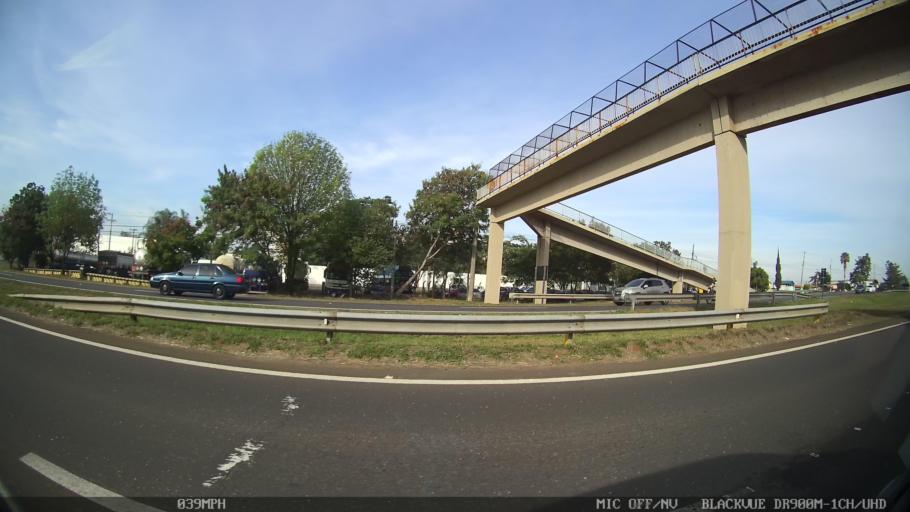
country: BR
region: Sao Paulo
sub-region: Piracicaba
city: Piracicaba
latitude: -22.6799
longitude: -47.7023
